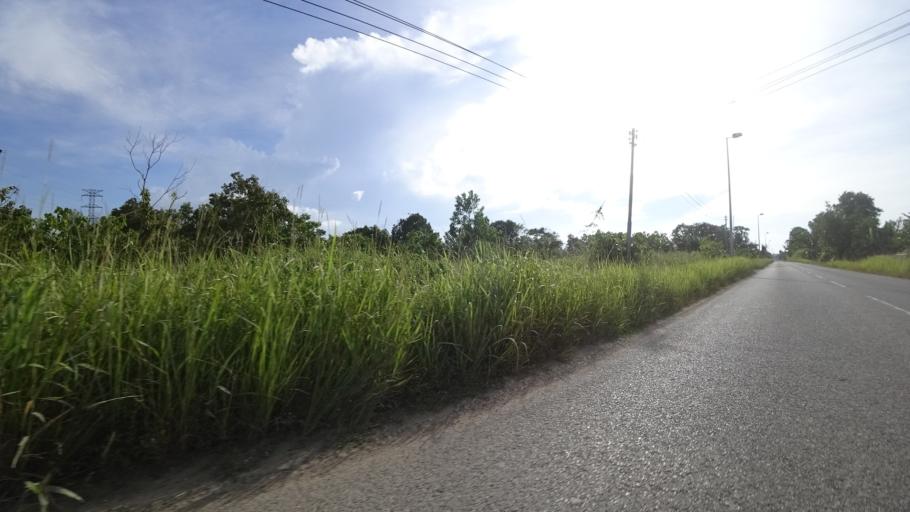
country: BN
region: Brunei and Muara
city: Bandar Seri Begawan
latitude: 4.8450
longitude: 114.8591
